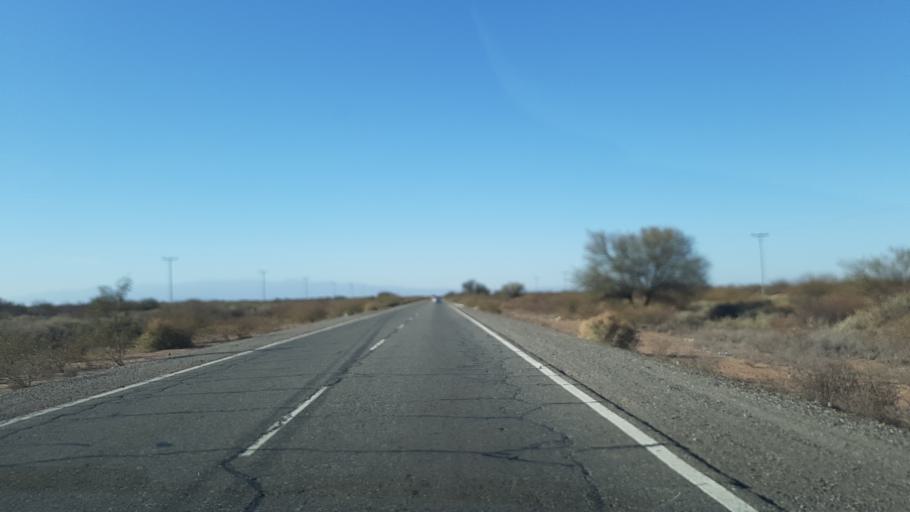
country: AR
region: San Juan
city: Caucete
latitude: -31.6199
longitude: -67.7317
